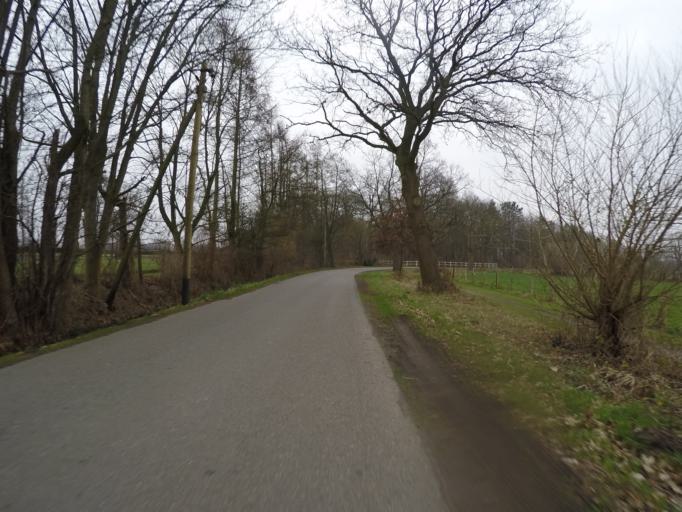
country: DE
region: Schleswig-Holstein
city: Tangstedt
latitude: 53.6903
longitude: 9.8550
